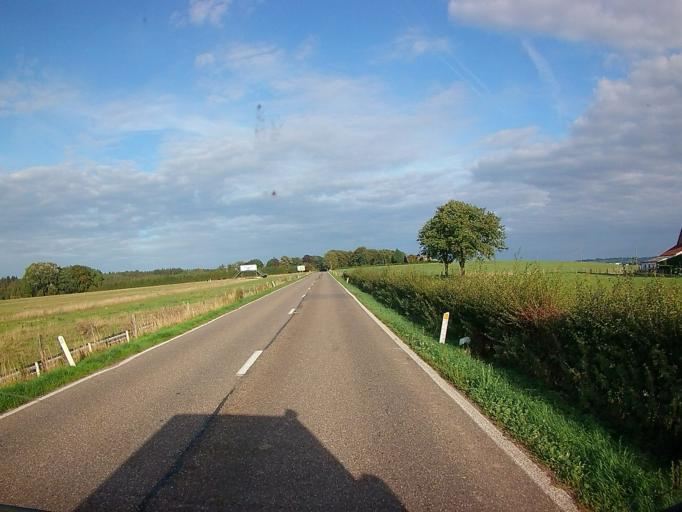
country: BE
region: Flanders
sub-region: Provincie Limburg
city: Sint-Pieters-Voeren
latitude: 50.7149
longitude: 5.8329
